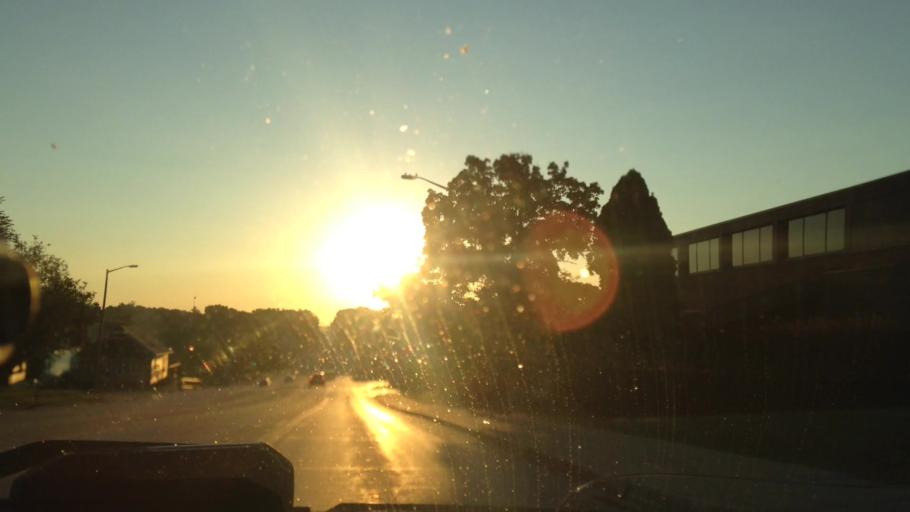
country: US
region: Wisconsin
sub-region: Washington County
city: West Bend
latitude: 43.4268
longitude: -88.1875
